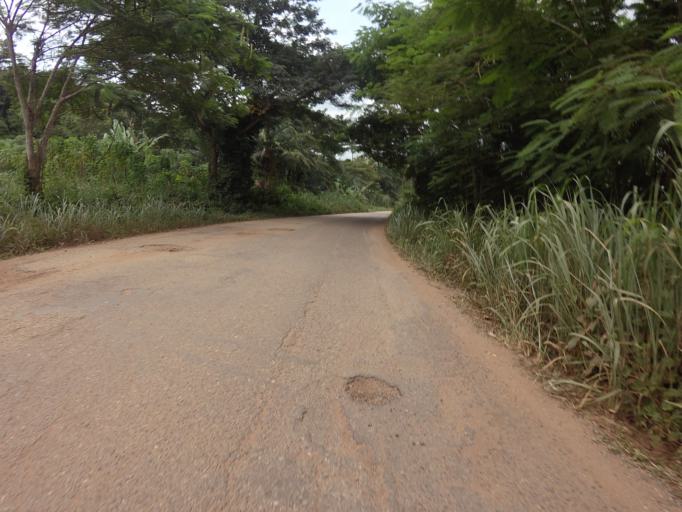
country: GH
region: Volta
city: Ho
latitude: 6.6455
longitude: 0.3374
